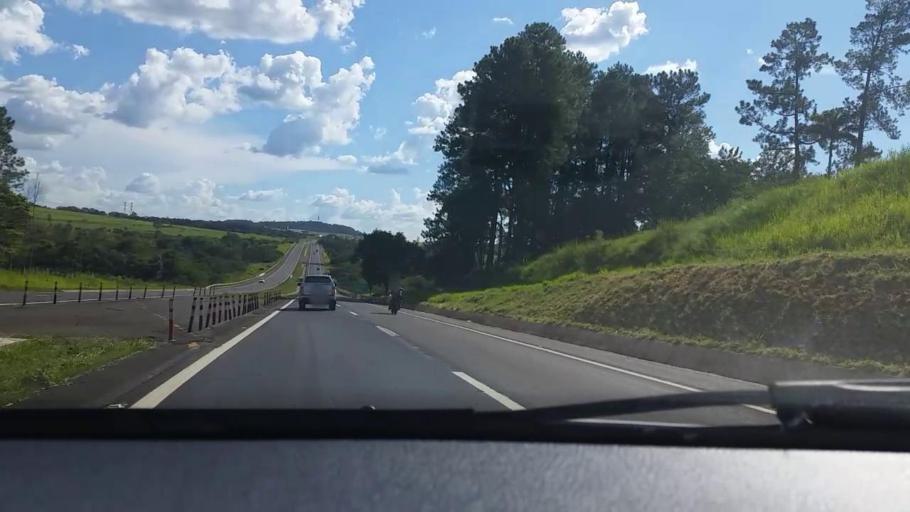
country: BR
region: Sao Paulo
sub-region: Bauru
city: Bauru
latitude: -22.4045
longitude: -49.0951
